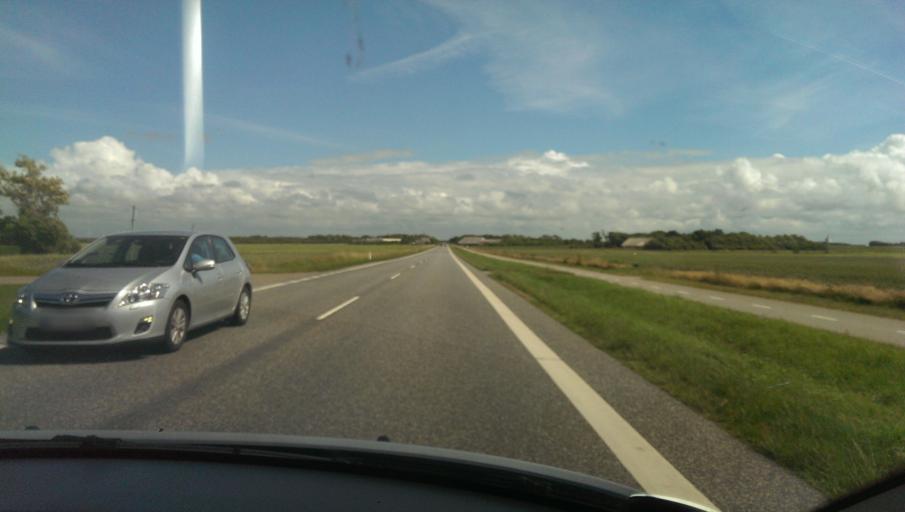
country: DK
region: Central Jutland
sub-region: Ringkobing-Skjern Kommune
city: Ringkobing
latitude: 56.1094
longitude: 8.1974
